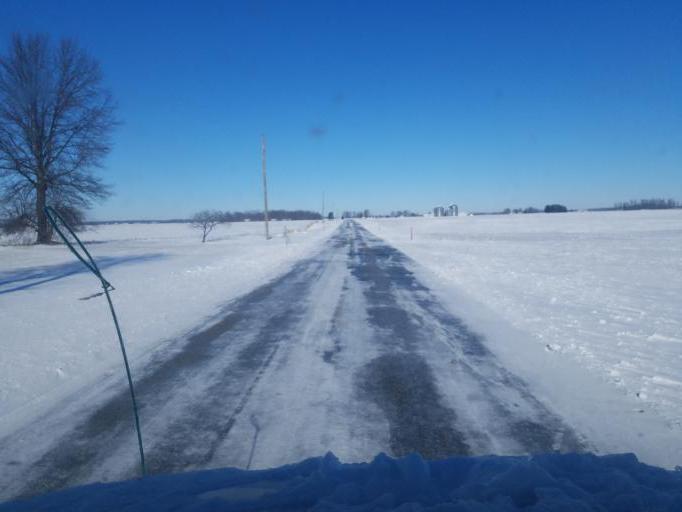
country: US
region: Ohio
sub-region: Delaware County
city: Delaware
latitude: 40.3076
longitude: -82.9886
